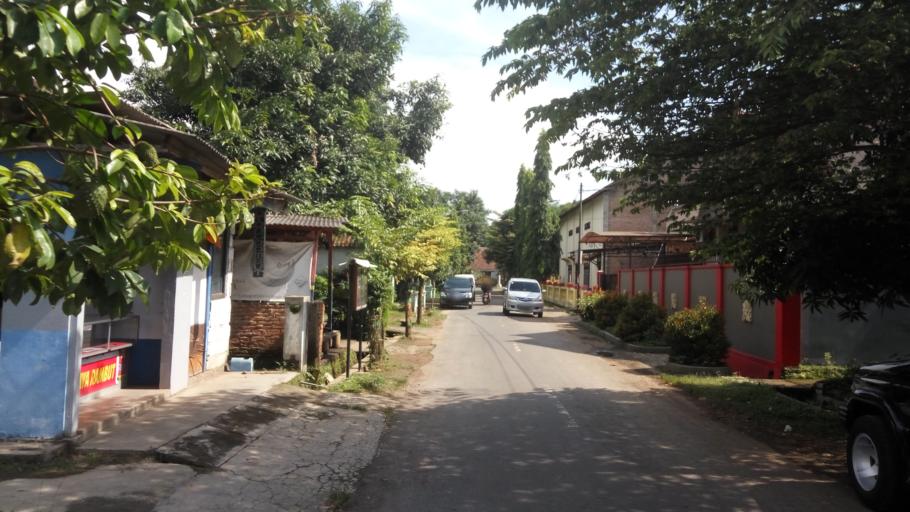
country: ID
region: Central Java
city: Ungaran
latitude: -7.1343
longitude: 110.4240
